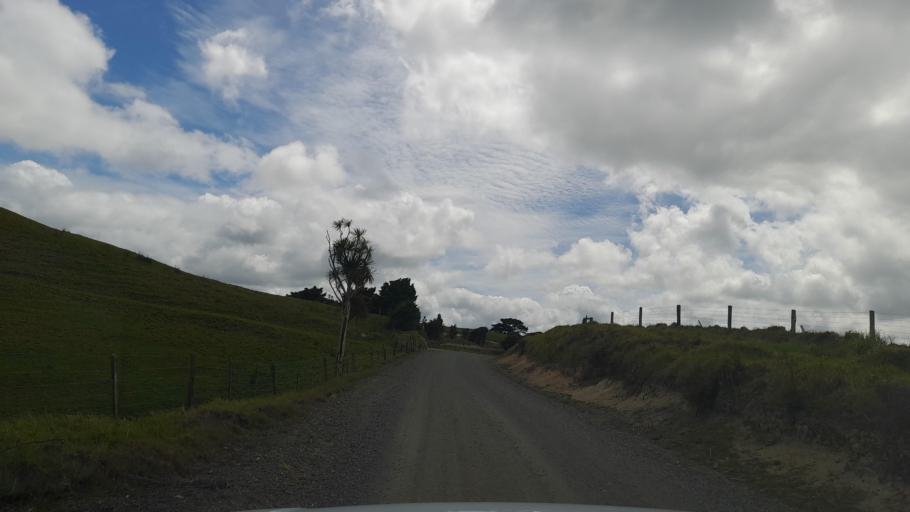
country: NZ
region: Auckland
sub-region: Auckland
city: Wellsford
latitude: -36.2037
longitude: 174.3371
